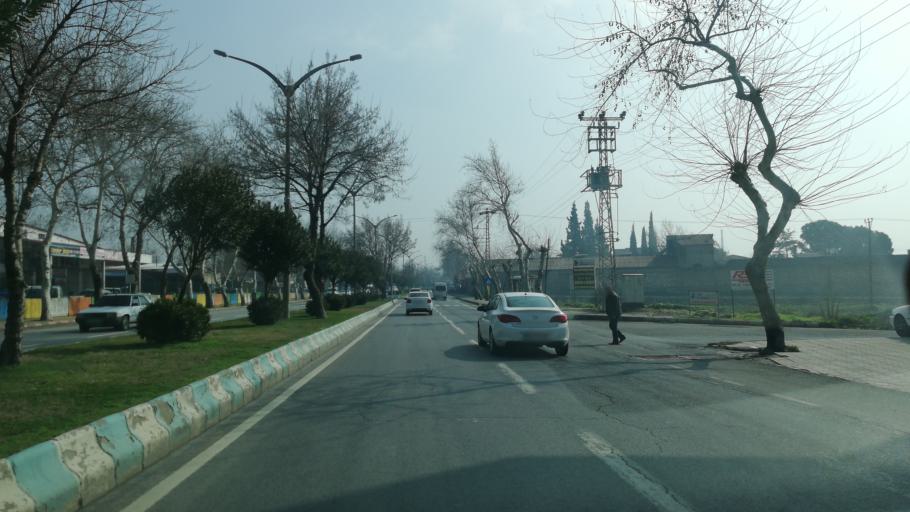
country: TR
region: Kahramanmaras
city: Kahramanmaras
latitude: 37.5637
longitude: 36.9523
